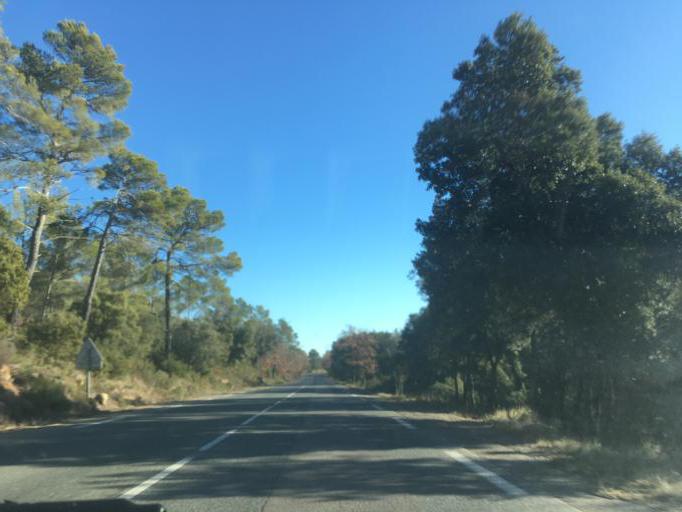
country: FR
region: Provence-Alpes-Cote d'Azur
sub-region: Departement du Var
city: Lorgues
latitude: 43.5457
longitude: 6.3323
